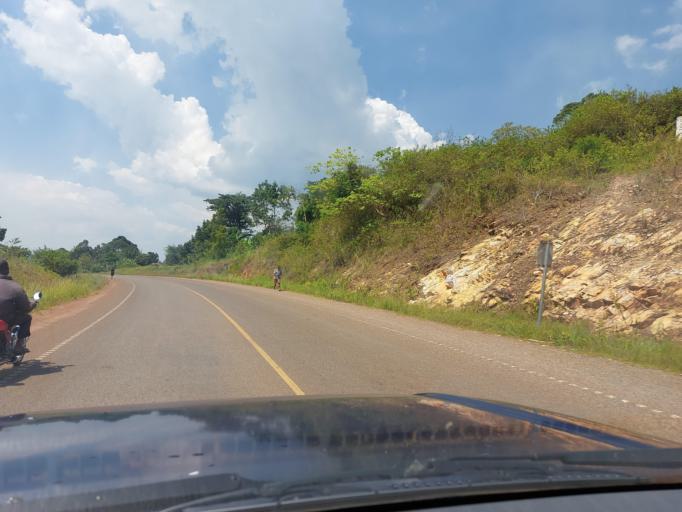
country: UG
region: Central Region
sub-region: Buikwe District
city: Buikwe
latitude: 0.2974
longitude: 33.0962
